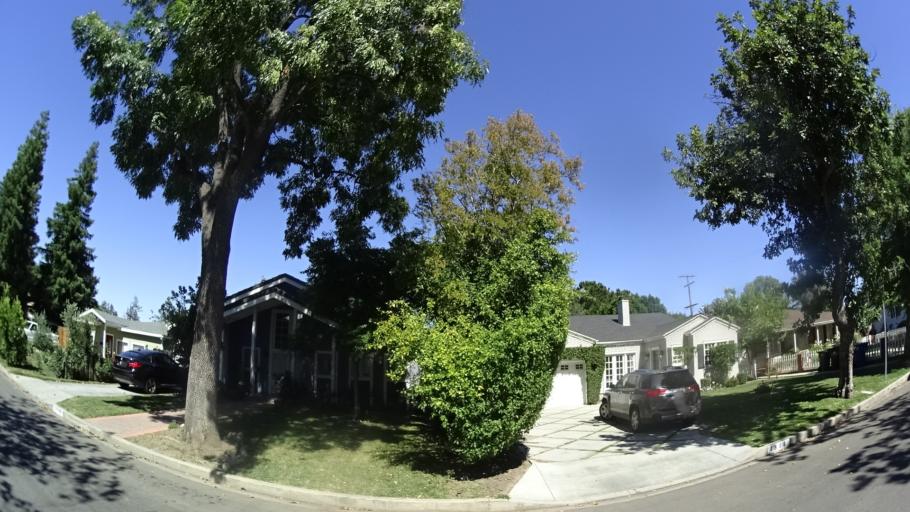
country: US
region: California
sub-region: Los Angeles County
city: Sherman Oaks
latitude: 34.1580
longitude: -118.4607
